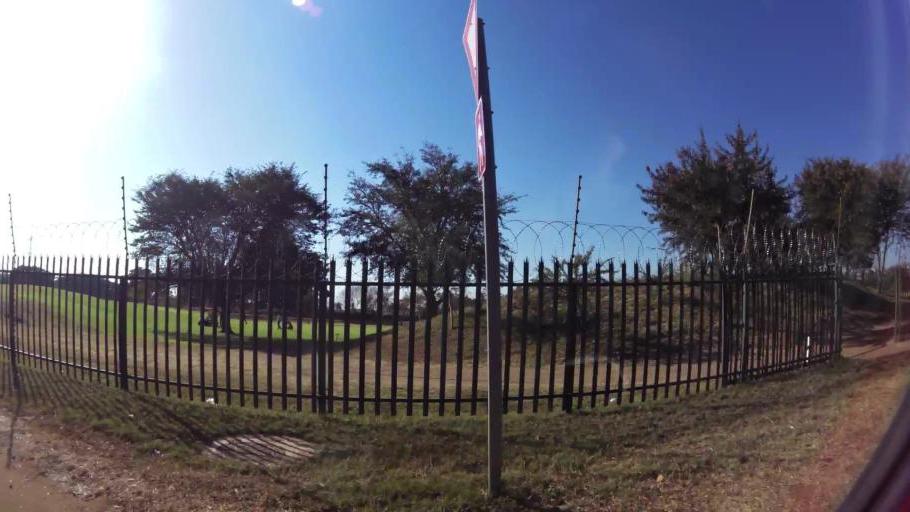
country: ZA
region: Gauteng
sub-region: City of Tshwane Metropolitan Municipality
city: Pretoria
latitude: -25.6577
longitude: 28.1435
